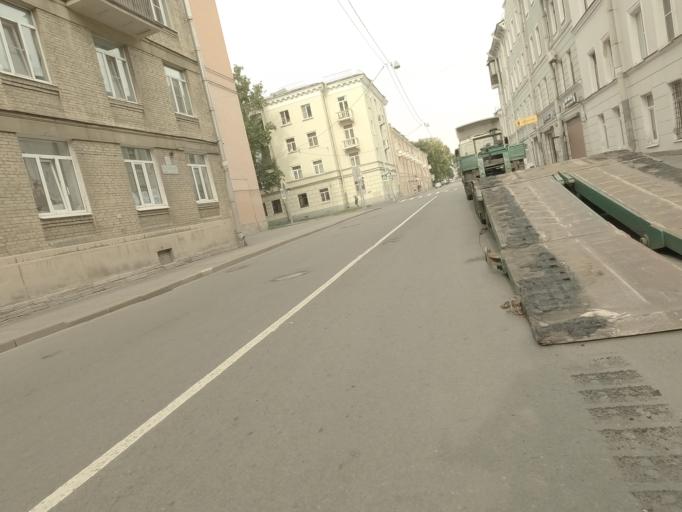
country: RU
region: St.-Petersburg
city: Admiralteisky
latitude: 59.8981
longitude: 30.2817
